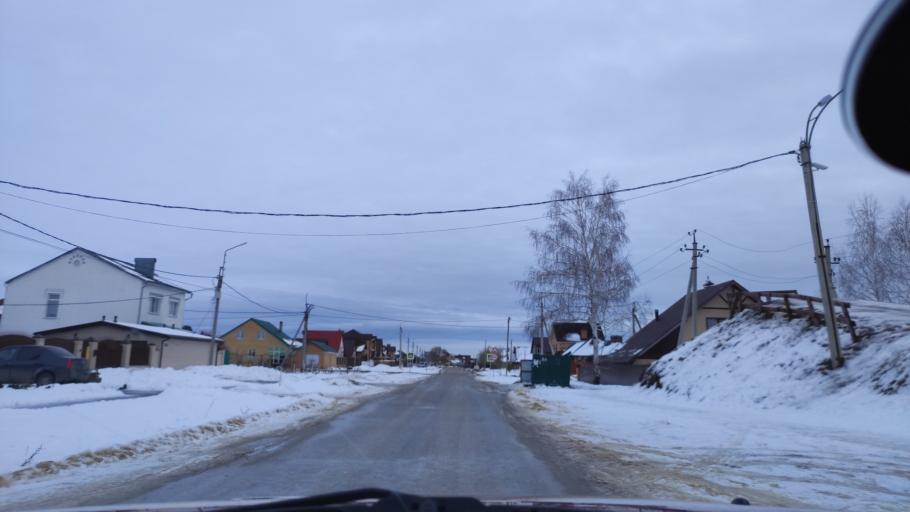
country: RU
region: Tambov
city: Tambov
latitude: 52.7678
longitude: 41.3734
